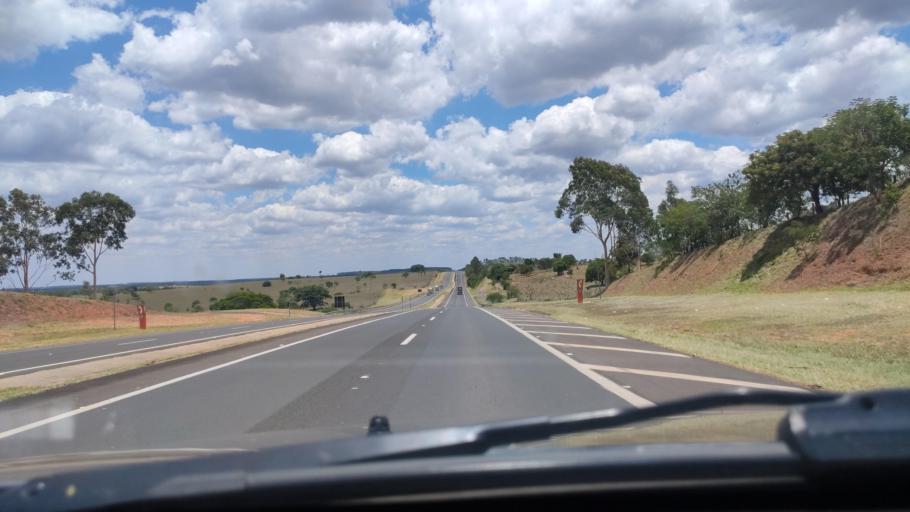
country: BR
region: Sao Paulo
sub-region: Duartina
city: Duartina
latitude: -22.4969
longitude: -49.2661
